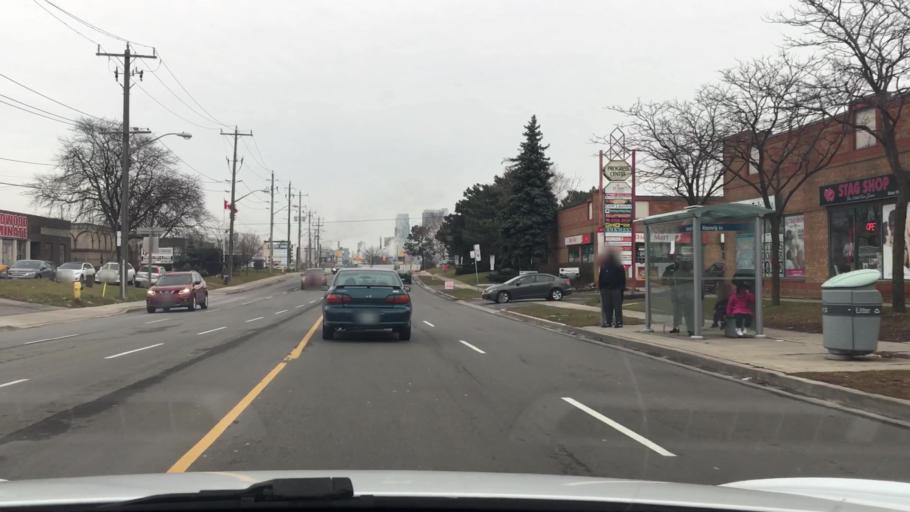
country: CA
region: Ontario
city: Scarborough
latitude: 43.7695
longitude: -79.2818
